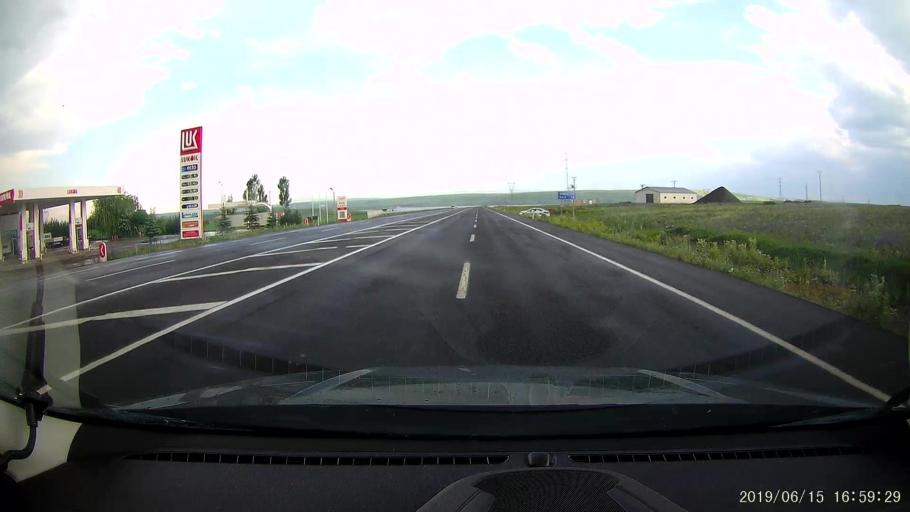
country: TR
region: Kars
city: Susuz
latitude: 40.7512
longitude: 43.1511
